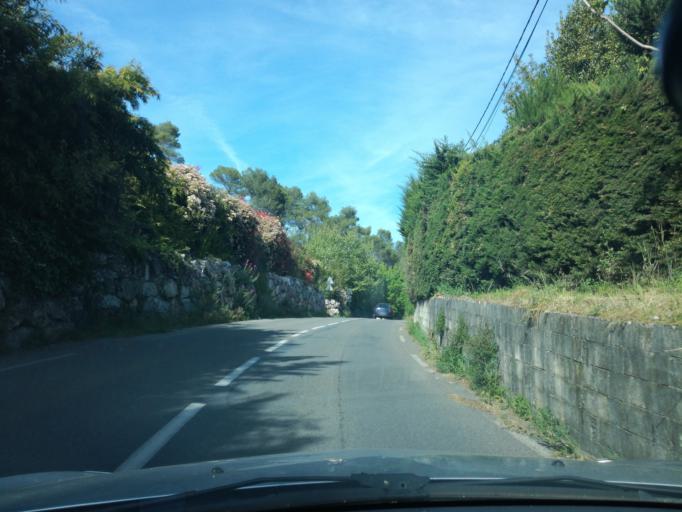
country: FR
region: Provence-Alpes-Cote d'Azur
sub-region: Departement des Alpes-Maritimes
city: La Roquette-sur-Siagne
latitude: 43.6195
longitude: 6.9480
